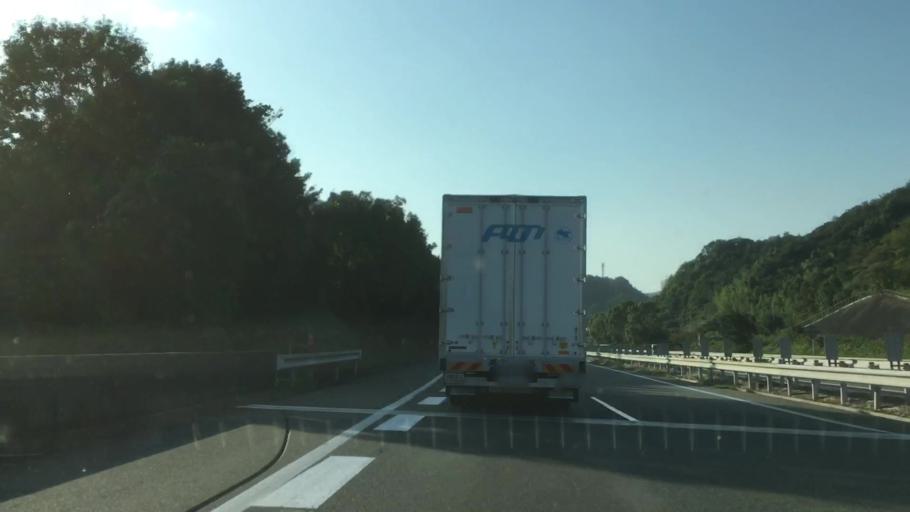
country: JP
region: Yamaguchi
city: Ogori-shimogo
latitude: 34.0856
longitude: 131.4693
